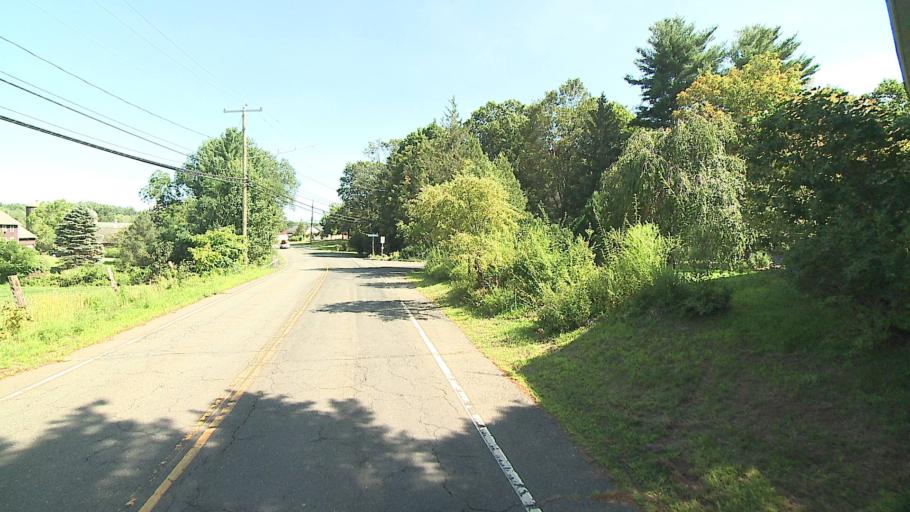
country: US
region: Connecticut
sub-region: Hartford County
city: West Simsbury
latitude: 41.8734
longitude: -72.8588
